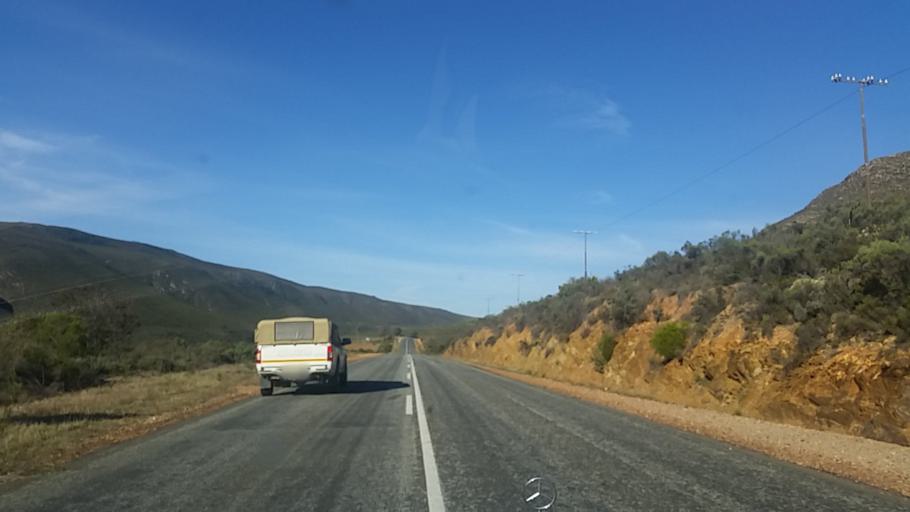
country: ZA
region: Western Cape
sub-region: Eden District Municipality
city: Knysna
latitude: -33.7464
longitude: 22.9857
